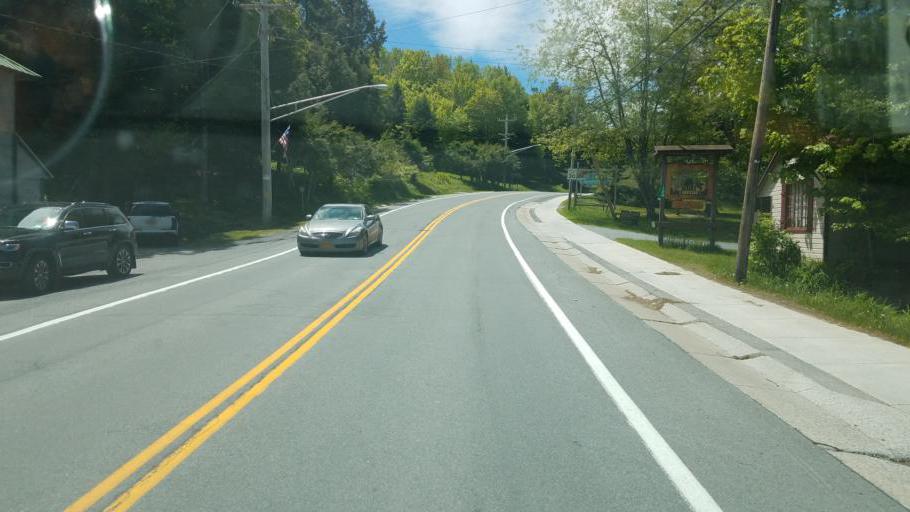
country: US
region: New York
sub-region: Hamilton County
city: Lake Pleasant
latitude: 43.7551
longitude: -74.7917
